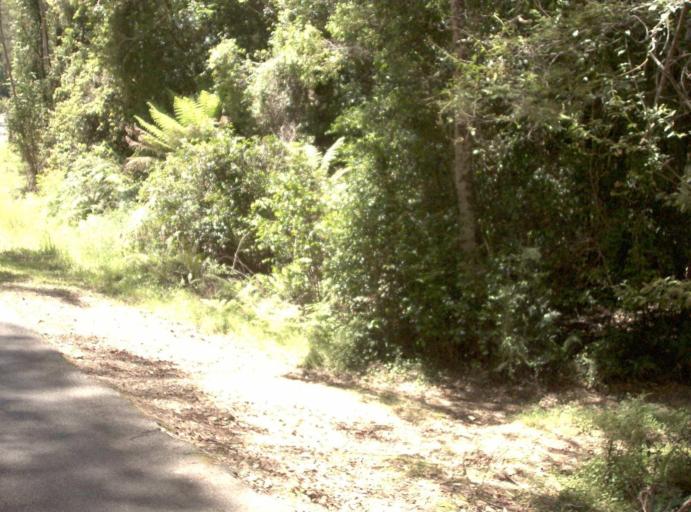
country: AU
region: New South Wales
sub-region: Bombala
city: Bombala
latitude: -37.4466
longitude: 148.9351
